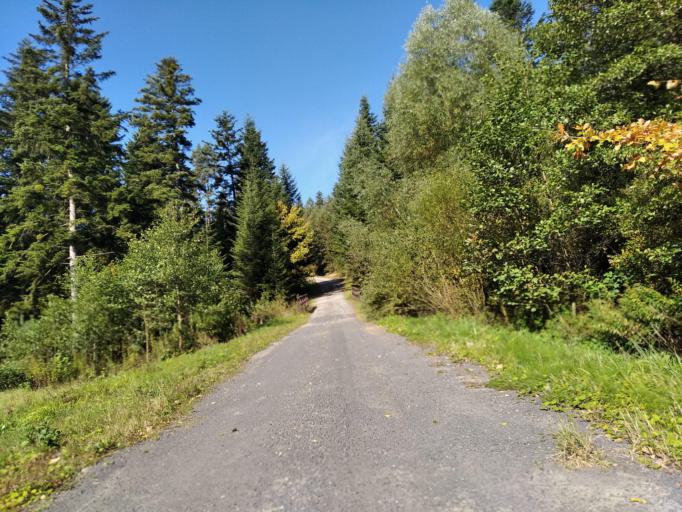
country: PL
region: Subcarpathian Voivodeship
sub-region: Powiat strzyzowski
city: Strzyzow
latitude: 49.8079
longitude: 21.8083
